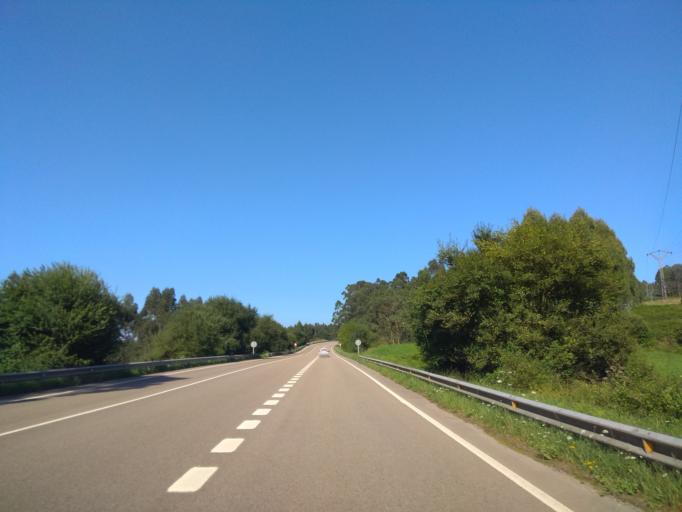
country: ES
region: Cantabria
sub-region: Provincia de Cantabria
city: Bareyo
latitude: 43.4709
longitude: -3.6361
